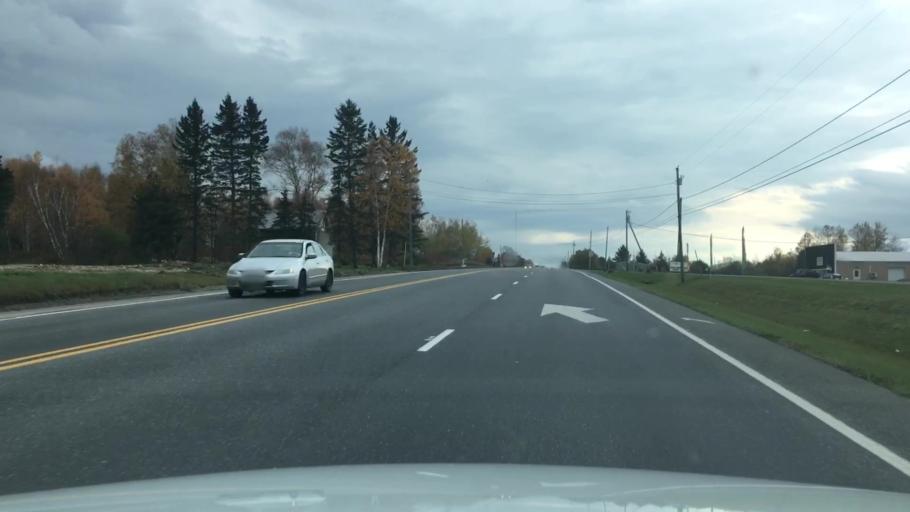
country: US
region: Maine
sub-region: Aroostook County
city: Caribou
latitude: 46.7799
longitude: -67.9892
